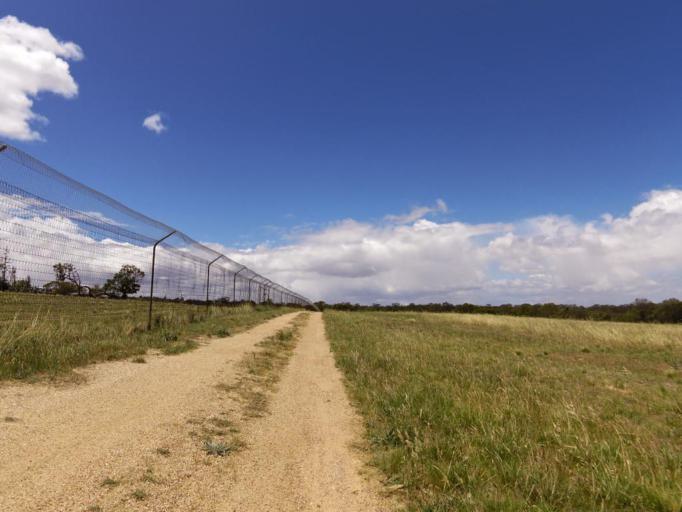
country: AU
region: Victoria
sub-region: Hume
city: Greenvale
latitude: -37.6556
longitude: 144.8520
